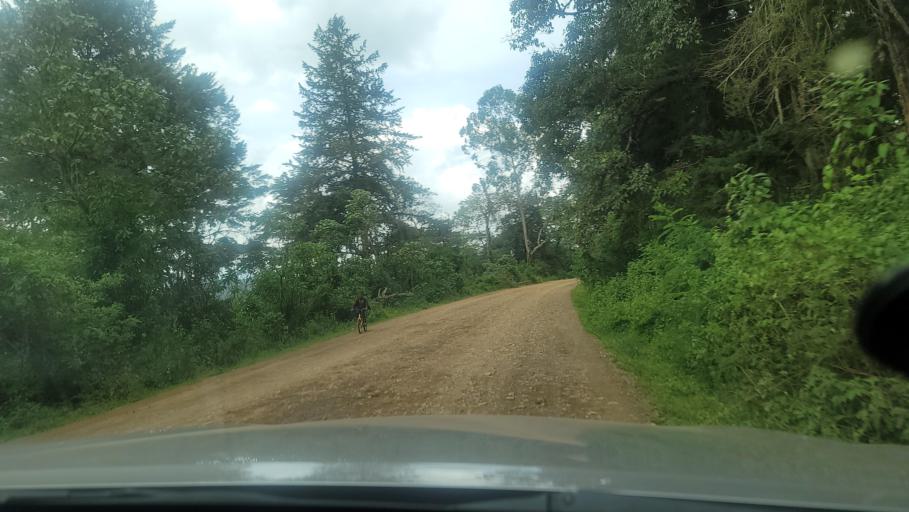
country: ET
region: Oromiya
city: Agaro
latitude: 7.7881
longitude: 36.4295
